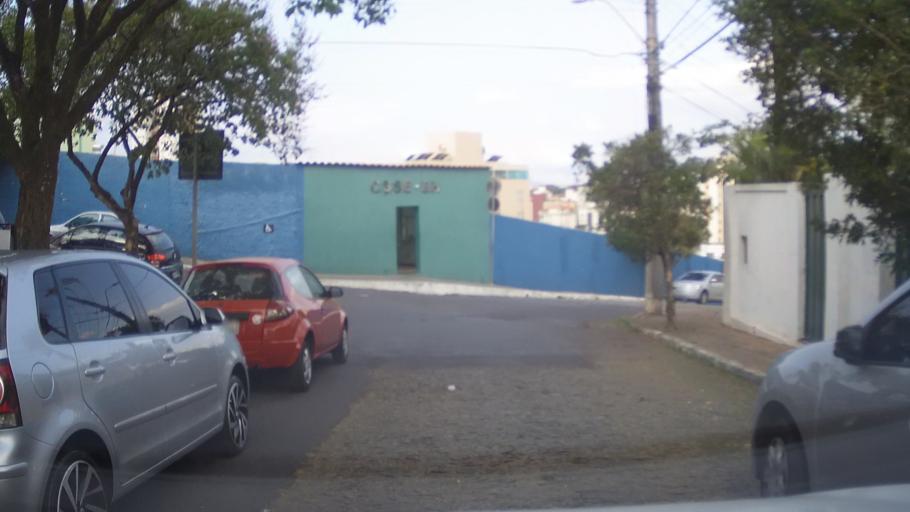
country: BR
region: Minas Gerais
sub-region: Belo Horizonte
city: Belo Horizonte
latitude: -19.8982
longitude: -43.9299
